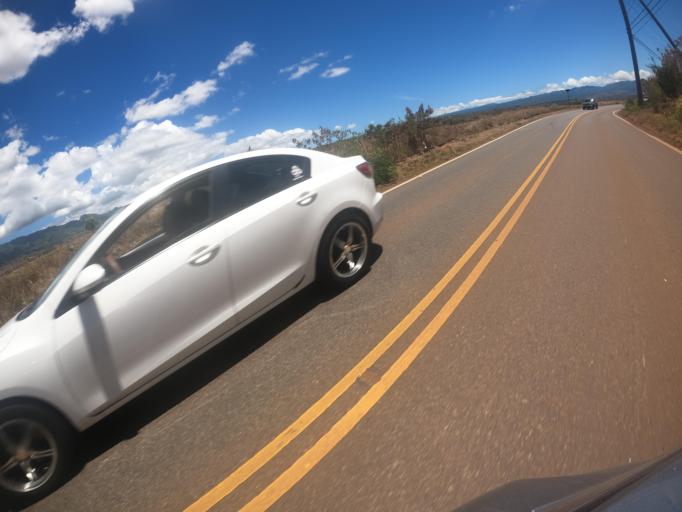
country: US
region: Hawaii
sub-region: Honolulu County
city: Royal Kunia
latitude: 21.3740
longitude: -158.0416
